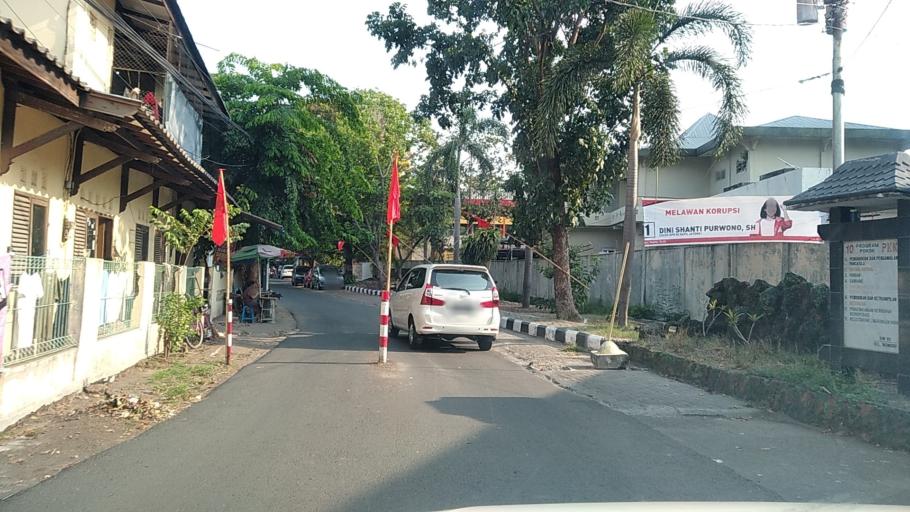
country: ID
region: Central Java
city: Semarang
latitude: -6.9966
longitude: 110.4293
